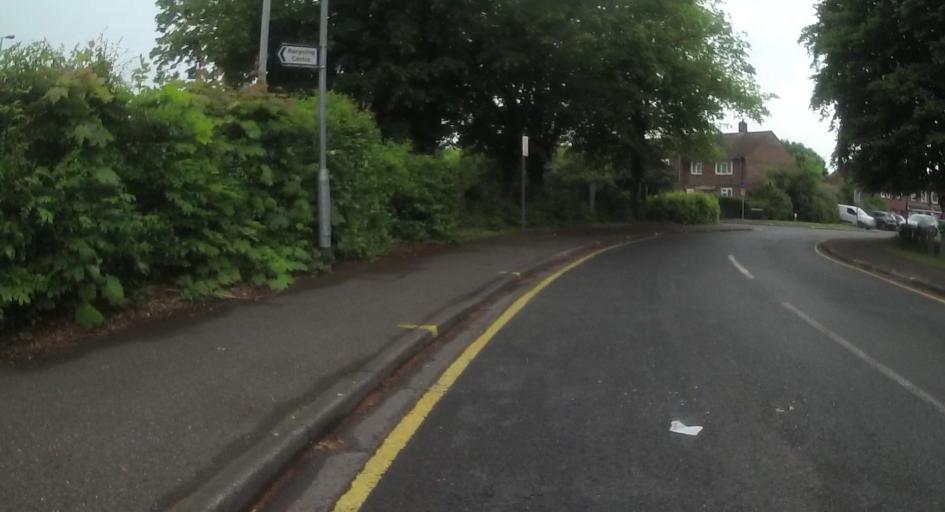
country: GB
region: England
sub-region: Bracknell Forest
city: Bracknell
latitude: 51.4194
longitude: -0.7511
